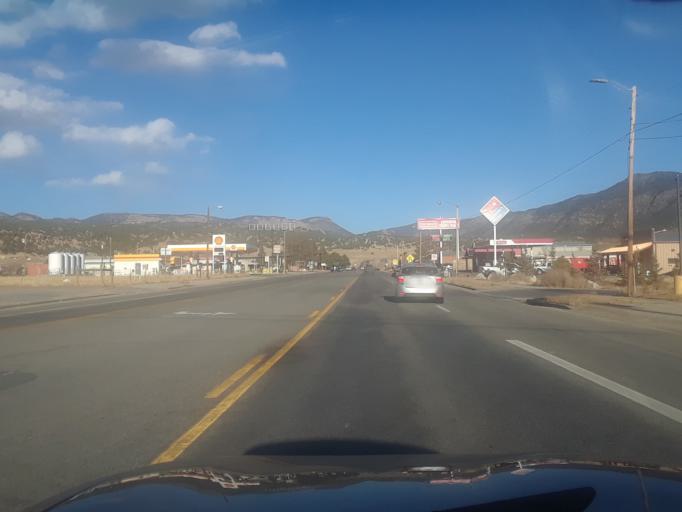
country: US
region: Colorado
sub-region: Chaffee County
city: Buena Vista
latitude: 38.8118
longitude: -106.1088
